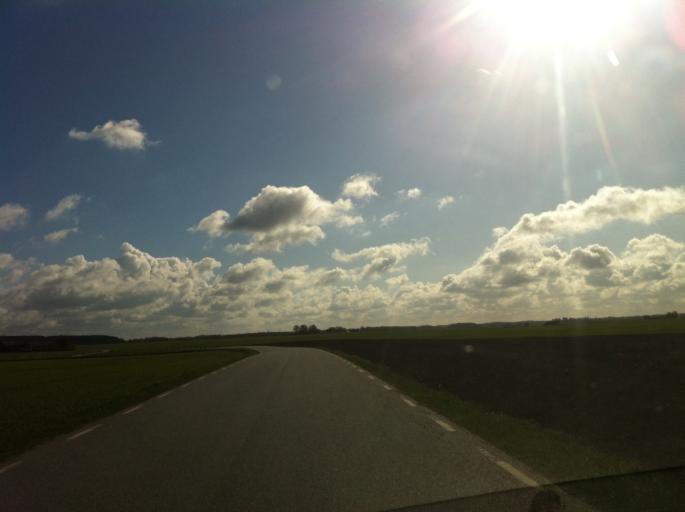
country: SE
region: Skane
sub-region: Eslovs Kommun
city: Eslov
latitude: 55.8639
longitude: 13.2398
